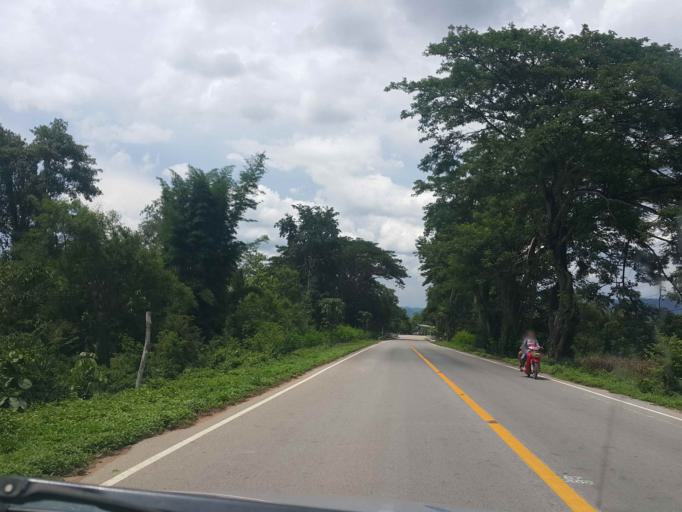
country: TH
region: Nan
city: Ban Luang
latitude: 18.8464
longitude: 100.4217
